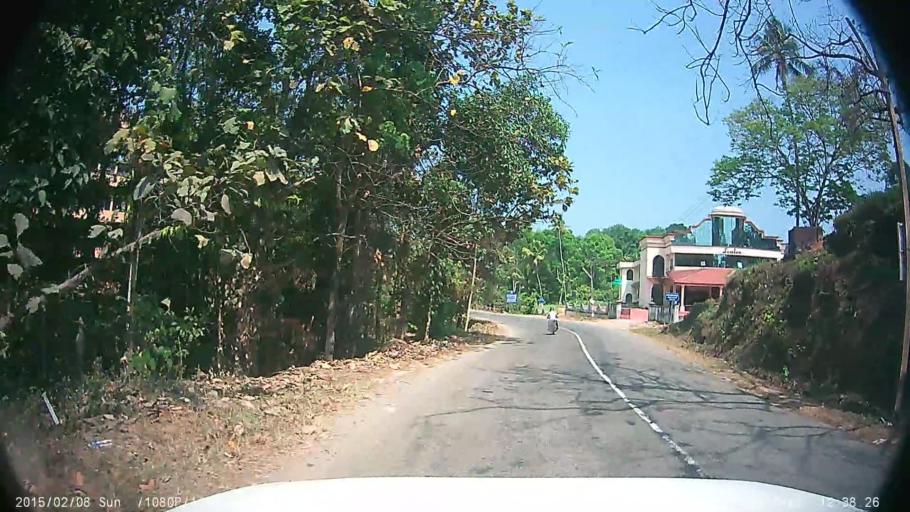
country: IN
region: Kerala
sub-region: Kottayam
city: Palackattumala
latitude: 9.7947
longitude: 76.5733
